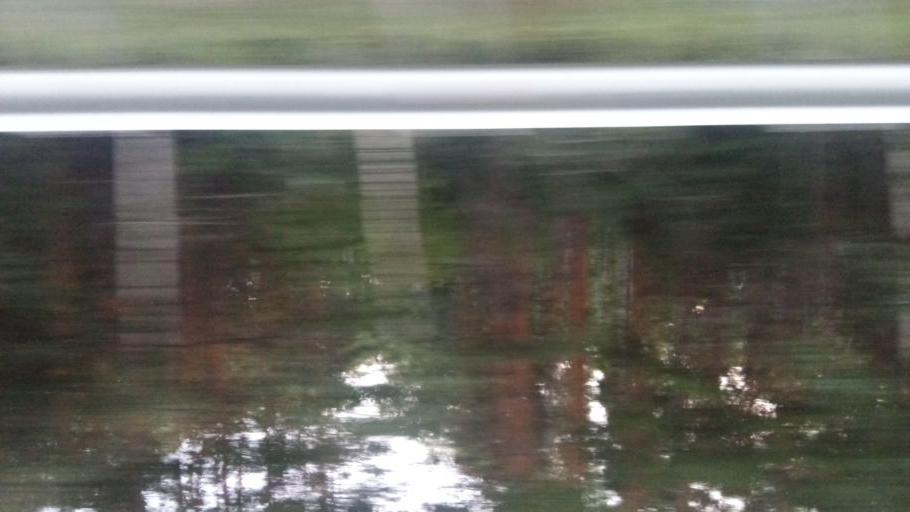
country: RU
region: Chelyabinsk
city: Sargazy
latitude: 54.9718
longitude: 61.2173
